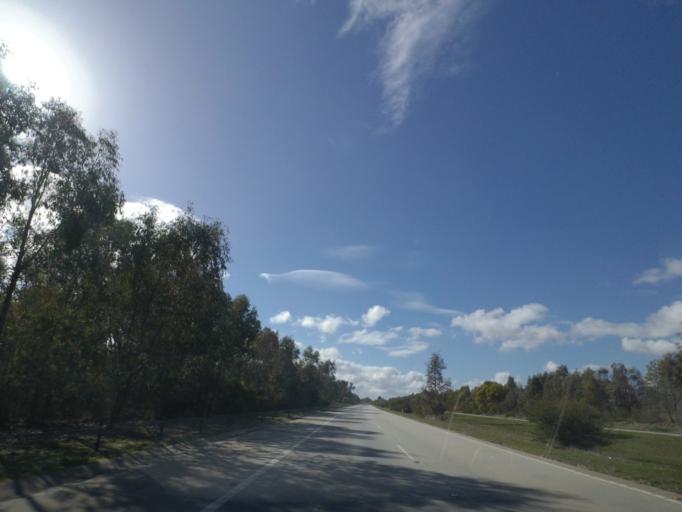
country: AU
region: New South Wales
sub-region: Albury Municipality
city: Lavington
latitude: -36.0264
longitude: 146.9787
